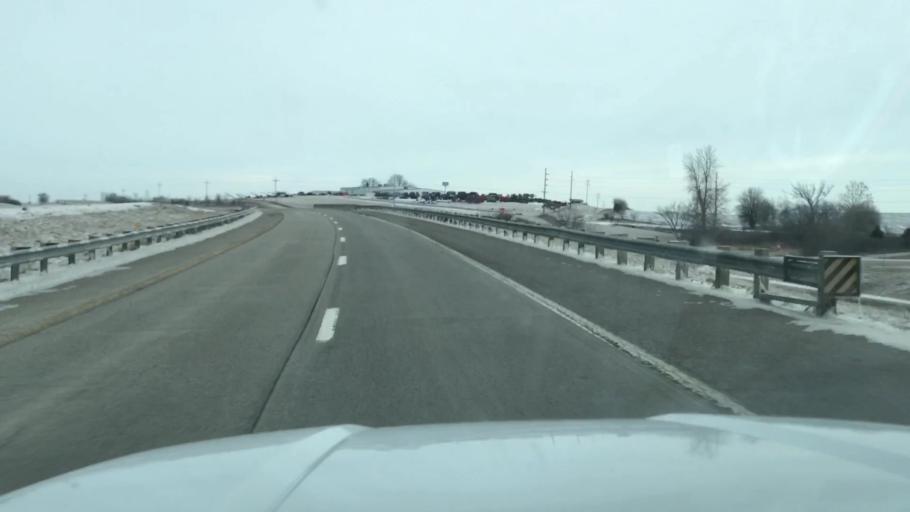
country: US
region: Missouri
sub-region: Andrew County
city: Savannah
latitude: 39.9606
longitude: -94.8606
